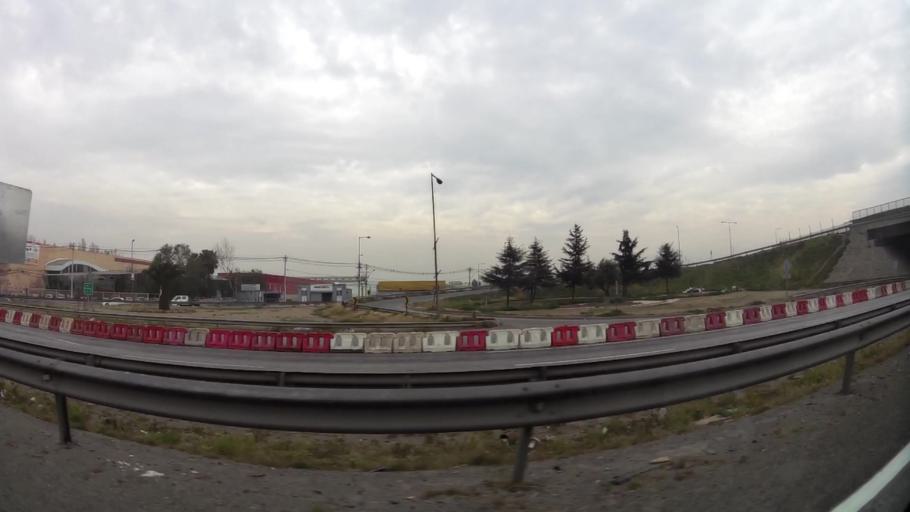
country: CL
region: Santiago Metropolitan
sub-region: Provincia de Chacabuco
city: Chicureo Abajo
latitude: -33.3344
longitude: -70.7145
